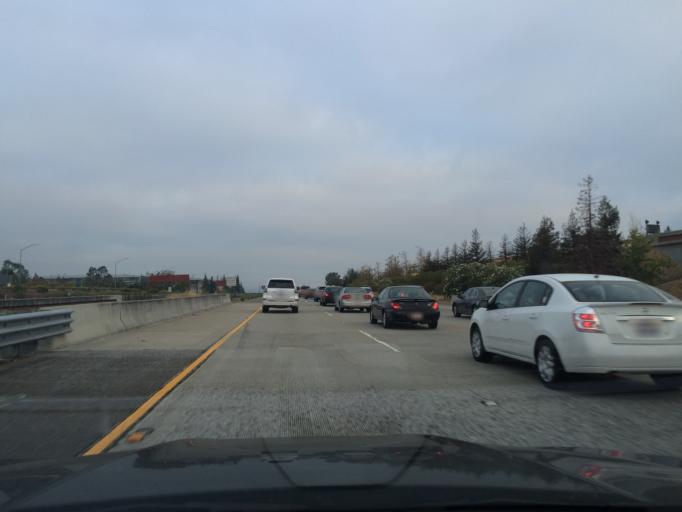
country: US
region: California
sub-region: Santa Clara County
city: Cambrian Park
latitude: 37.2564
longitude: -121.9573
